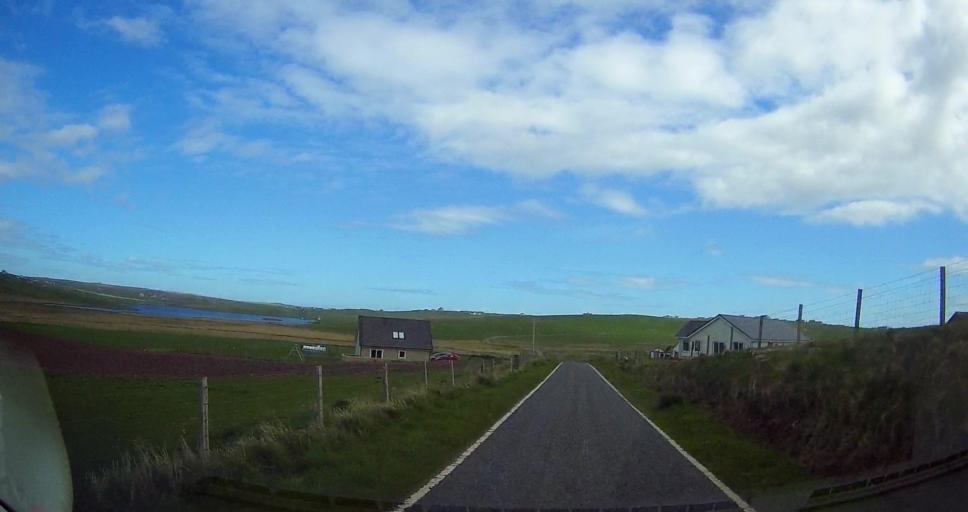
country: GB
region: Scotland
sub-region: Shetland Islands
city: Sandwick
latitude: 59.9237
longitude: -1.3326
